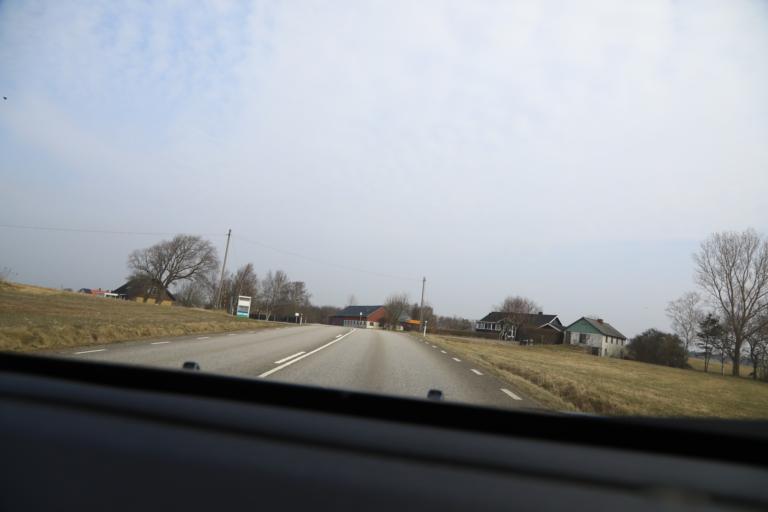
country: SE
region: Halland
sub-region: Kungsbacka Kommun
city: Frillesas
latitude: 57.2664
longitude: 12.1794
